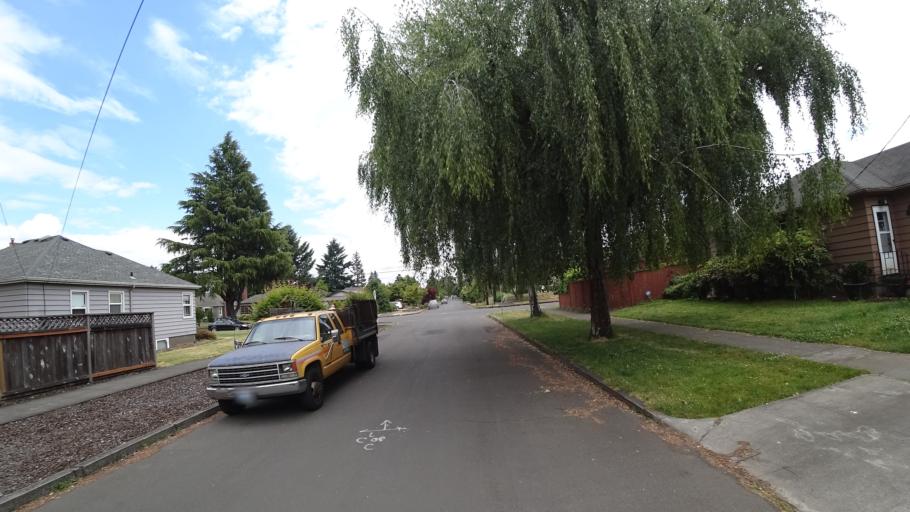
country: US
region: Oregon
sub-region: Washington County
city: West Haven
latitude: 45.5825
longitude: -122.7317
